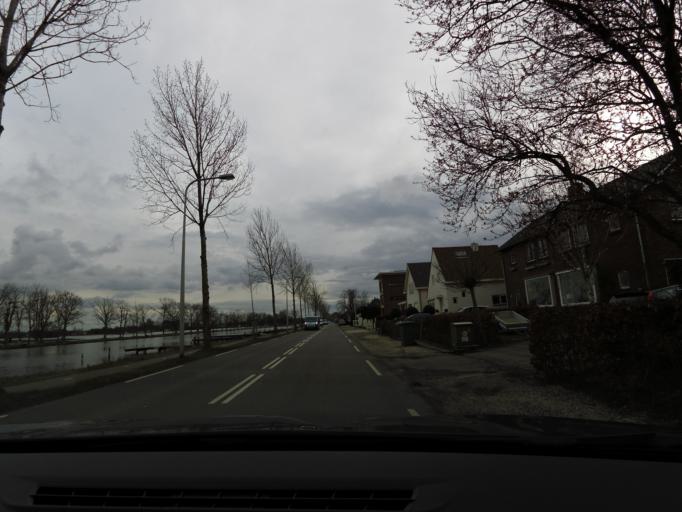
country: NL
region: South Holland
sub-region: Bodegraven-Reeuwijk
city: Reeuwijk
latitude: 52.0344
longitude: 4.7194
